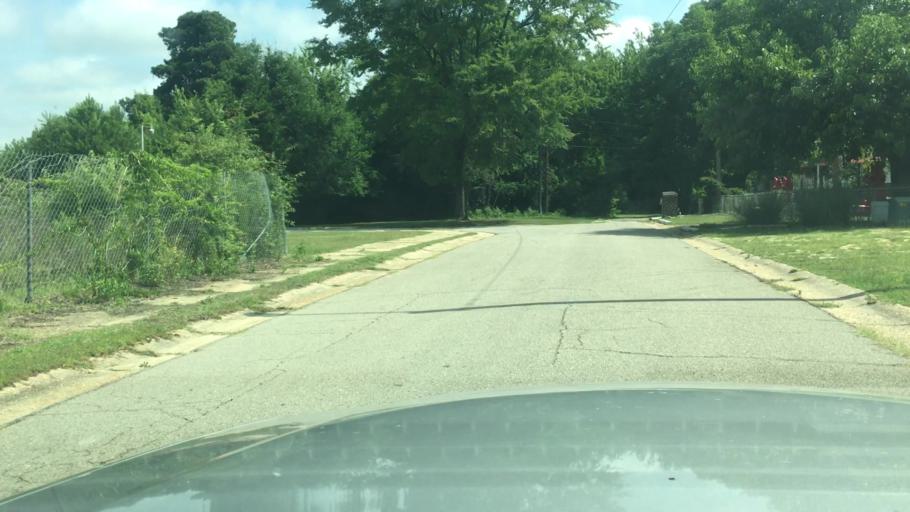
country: US
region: North Carolina
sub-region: Cumberland County
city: Fayetteville
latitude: 35.0261
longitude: -78.9037
